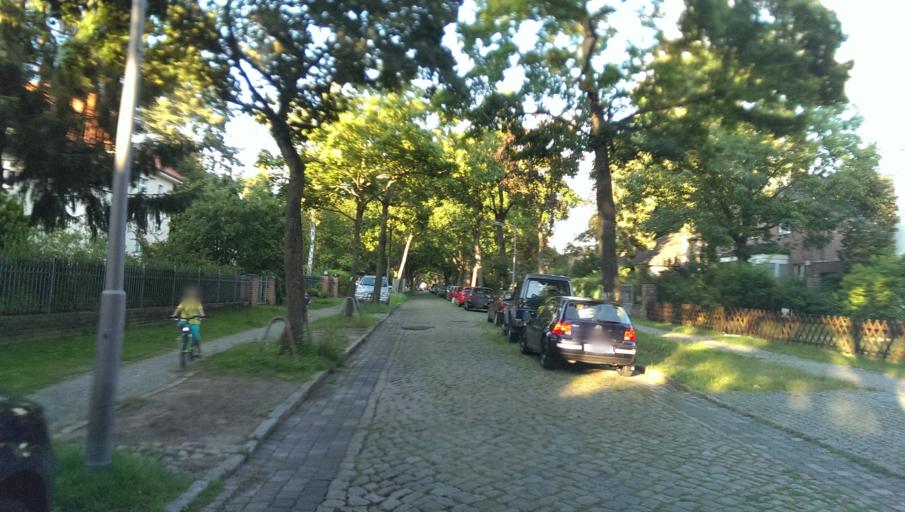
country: DE
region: Berlin
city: Lankwitz
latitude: 52.4388
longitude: 13.3343
